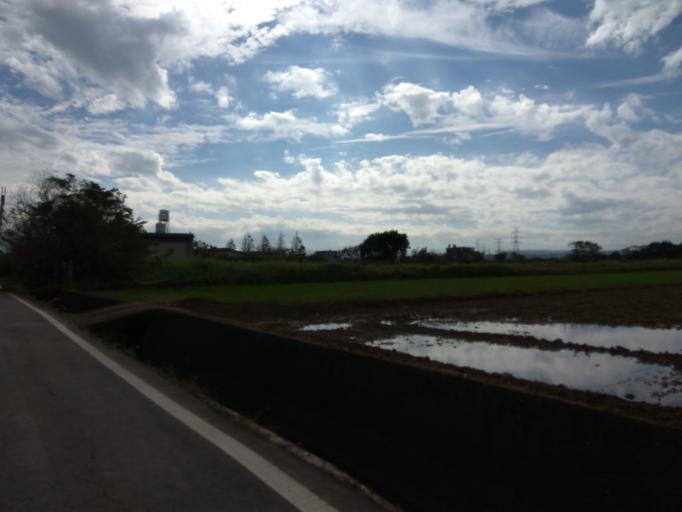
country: TW
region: Taiwan
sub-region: Hsinchu
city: Zhubei
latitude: 24.9533
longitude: 121.1071
